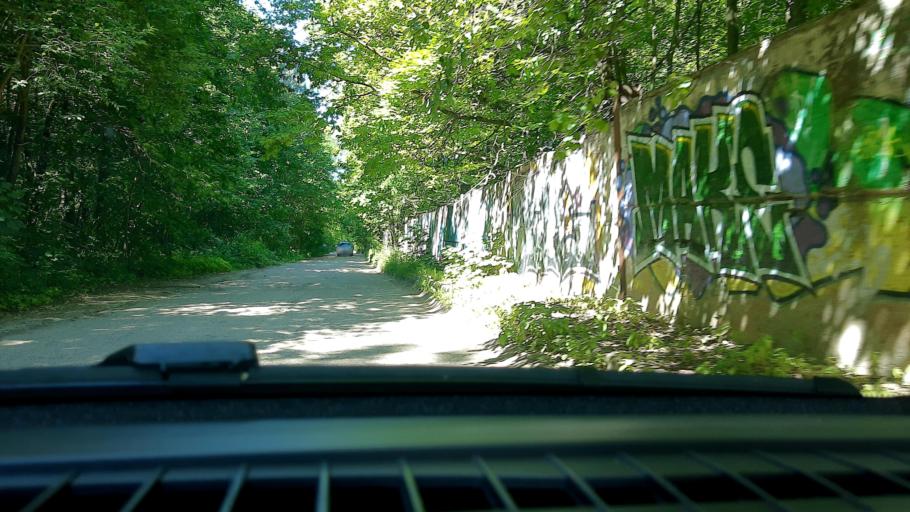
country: RU
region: Nizjnij Novgorod
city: Nizhniy Novgorod
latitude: 56.2286
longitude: 43.9357
